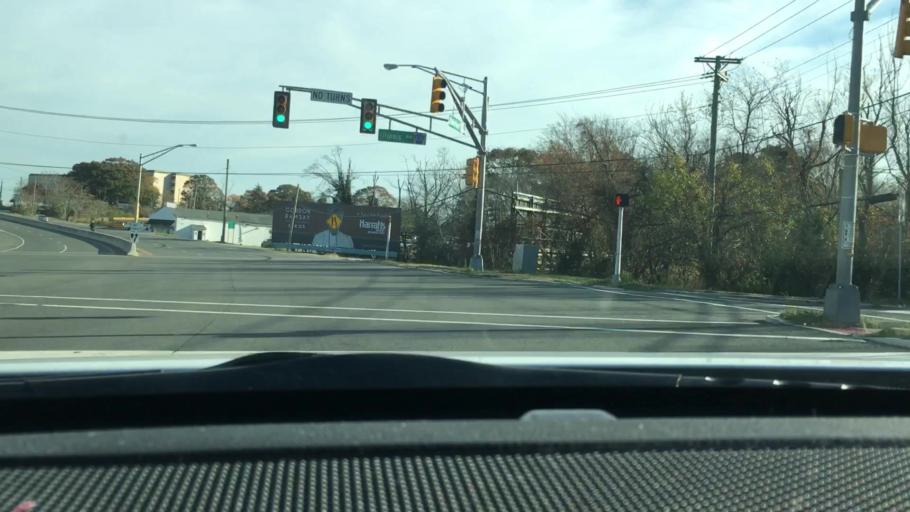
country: US
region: New Jersey
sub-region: Atlantic County
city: Absecon
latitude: 39.4201
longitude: -74.4974
